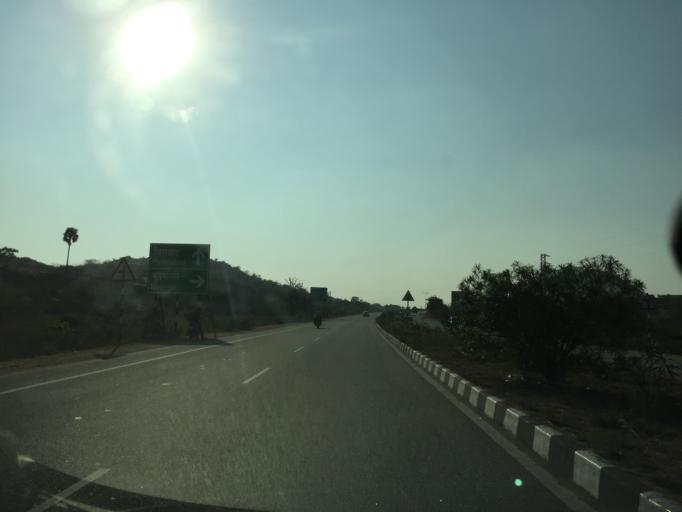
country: IN
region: Telangana
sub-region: Nalgonda
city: Bhongir
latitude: 17.5144
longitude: 78.9121
